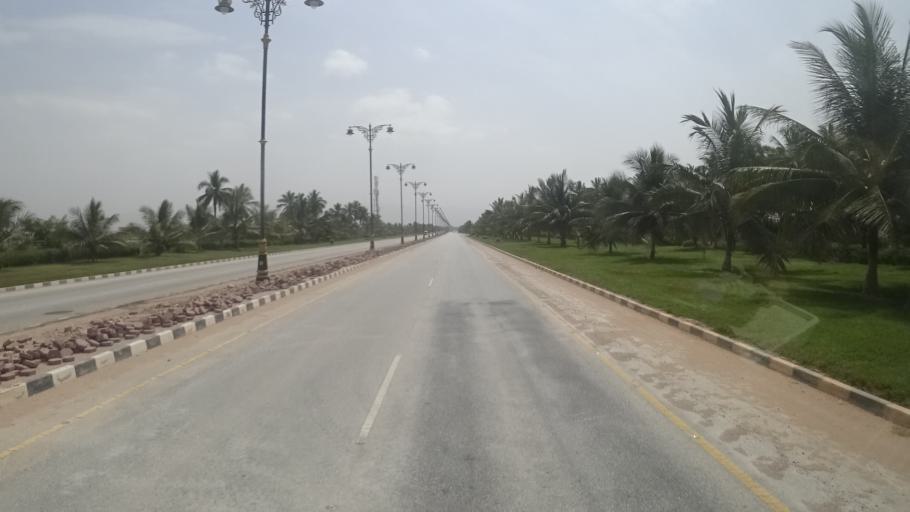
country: OM
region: Zufar
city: Salalah
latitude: 17.0417
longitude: 54.2033
